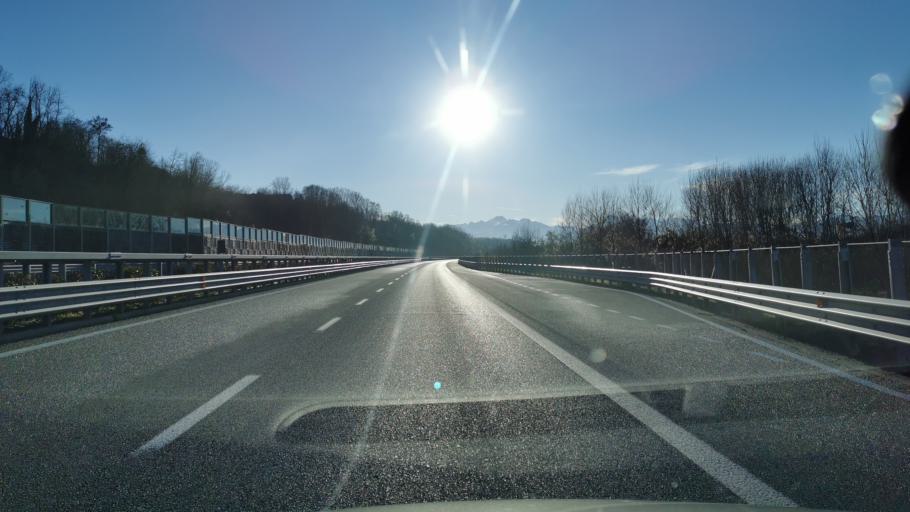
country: IT
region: Piedmont
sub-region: Provincia di Cuneo
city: Montanera
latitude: 44.4634
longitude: 7.6628
